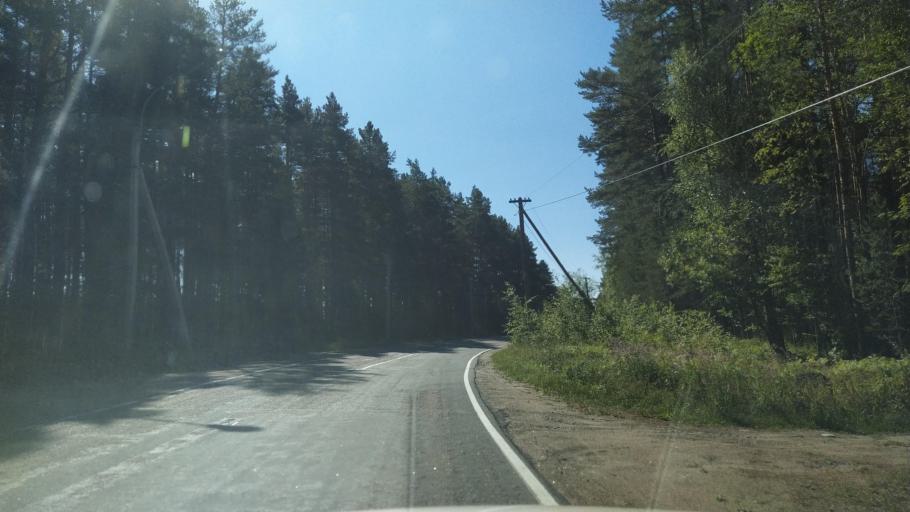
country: RU
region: Leningrad
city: Priozersk
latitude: 60.9677
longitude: 30.2861
